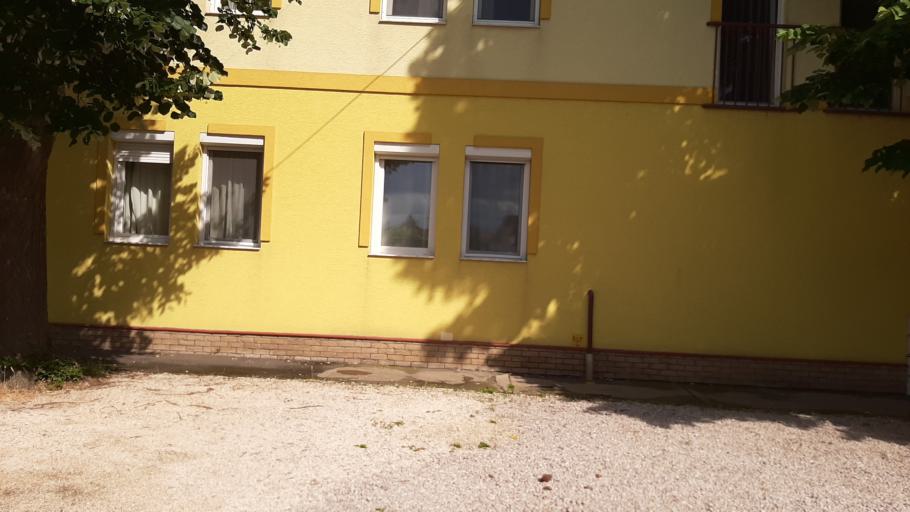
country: HU
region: Csongrad
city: Szeged
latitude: 46.2328
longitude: 20.1302
